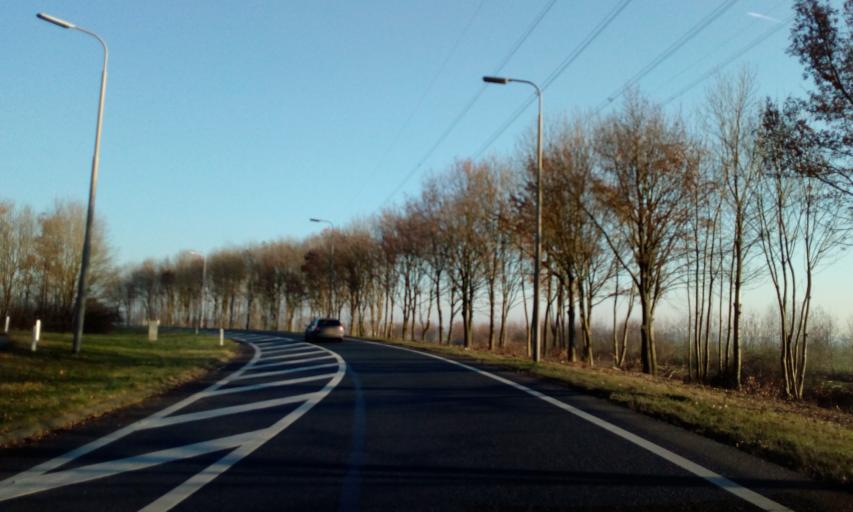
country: NL
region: Utrecht
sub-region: Gemeente Woerden
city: Woerden
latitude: 52.0704
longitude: 4.9048
